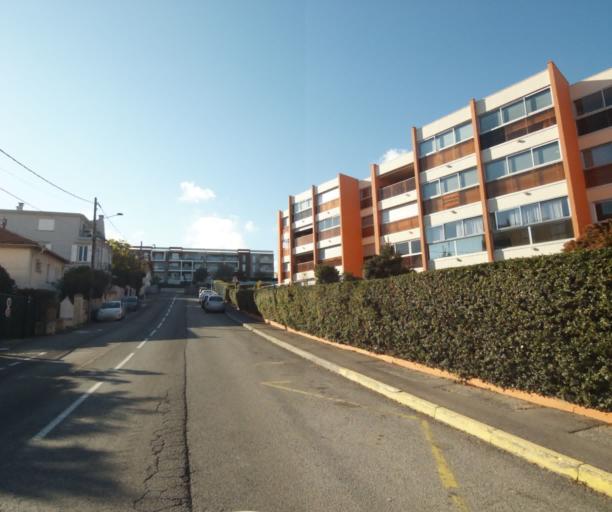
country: FR
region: Provence-Alpes-Cote d'Azur
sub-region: Departement des Alpes-Maritimes
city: Antibes
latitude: 43.5942
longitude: 7.1212
